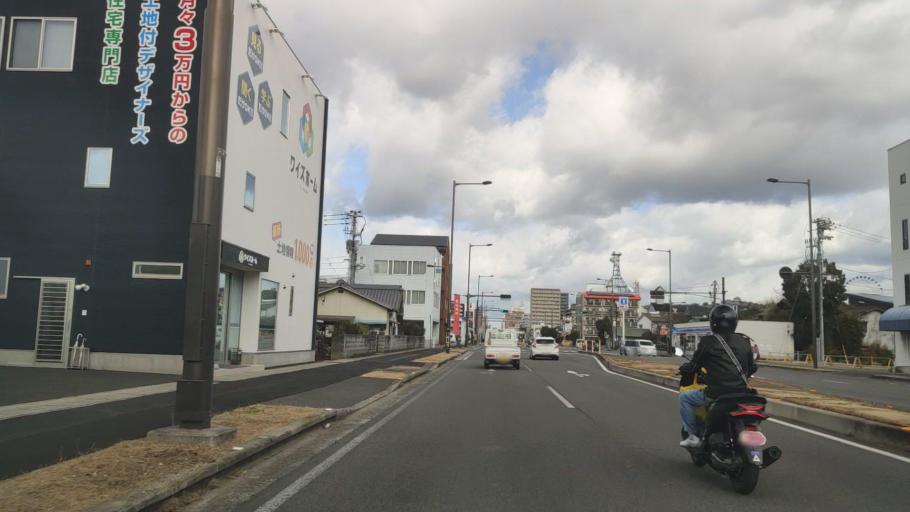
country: JP
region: Ehime
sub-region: Shikoku-chuo Shi
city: Matsuyama
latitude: 33.8284
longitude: 132.7588
